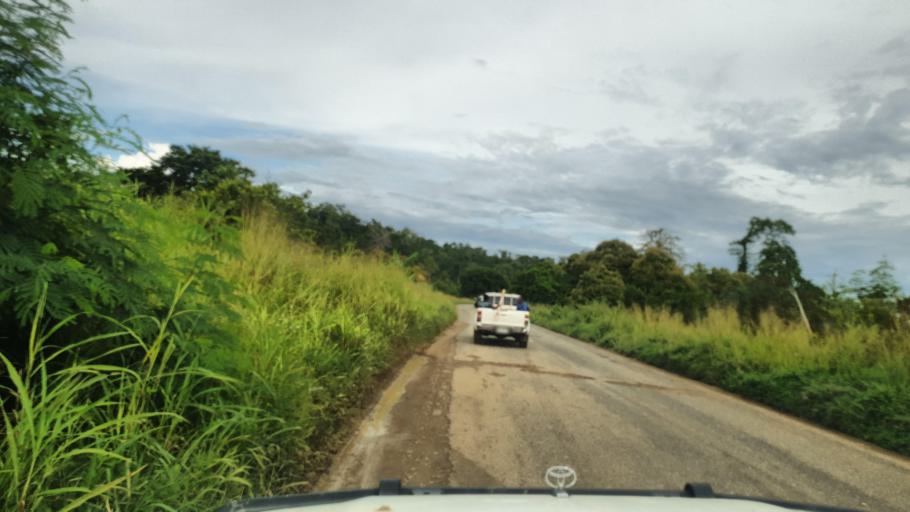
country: PG
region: Gulf
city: Kerema
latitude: -8.3380
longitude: 146.3266
